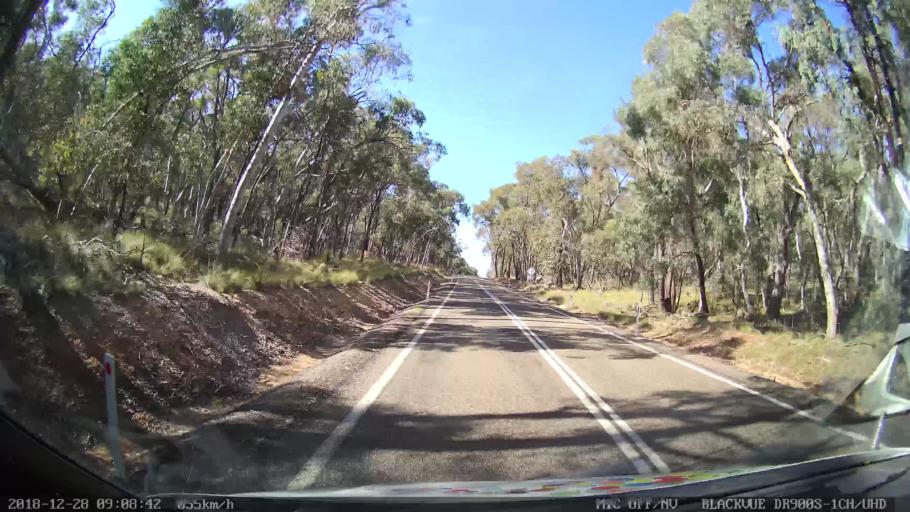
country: AU
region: New South Wales
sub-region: Upper Lachlan Shire
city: Crookwell
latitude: -34.2143
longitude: 149.3373
